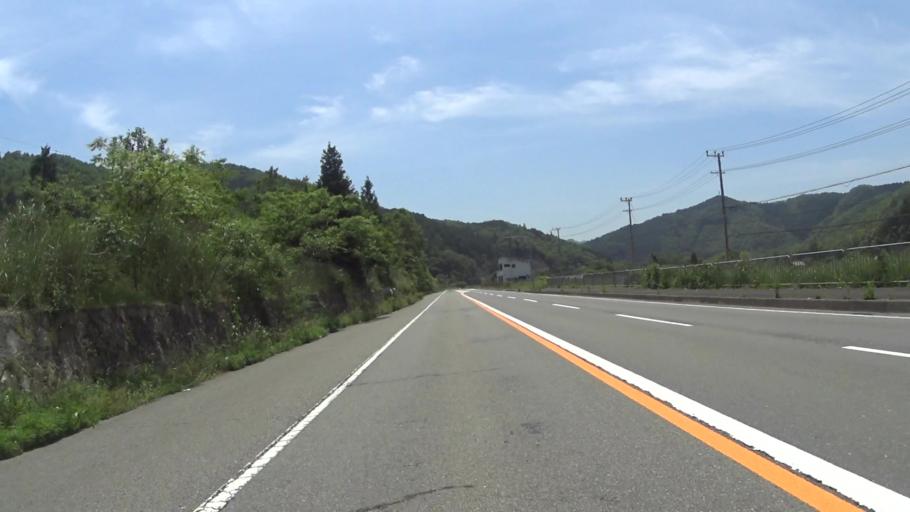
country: JP
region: Kyoto
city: Ayabe
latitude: 35.2078
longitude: 135.2686
